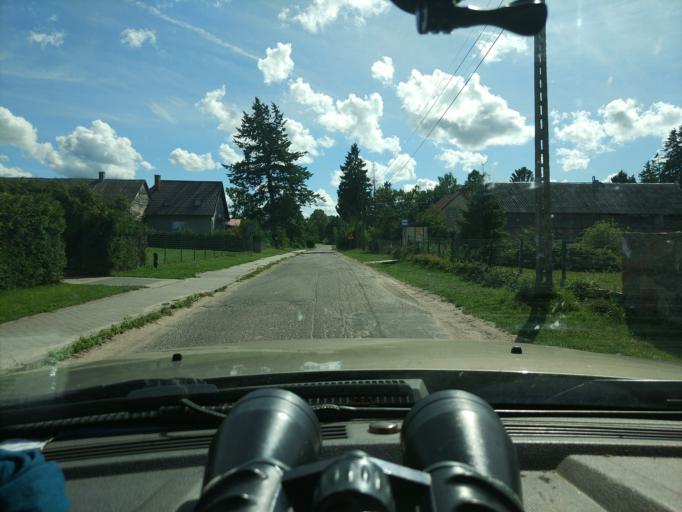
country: PL
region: Pomeranian Voivodeship
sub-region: Powiat wejherowski
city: Choczewo
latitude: 54.7694
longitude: 17.7939
